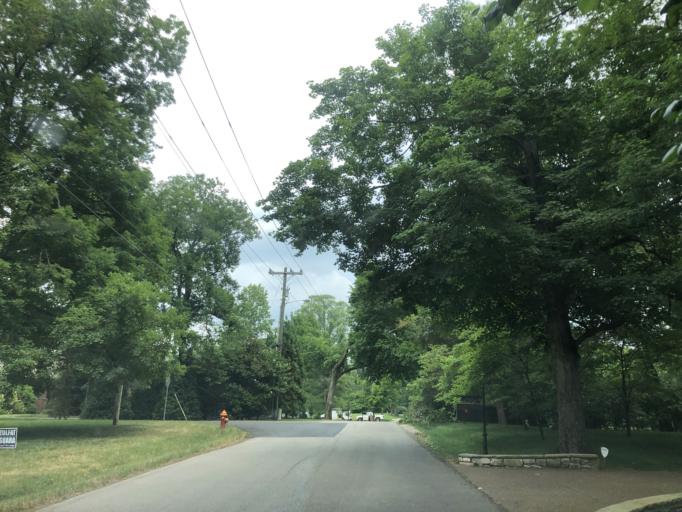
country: US
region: Tennessee
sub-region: Davidson County
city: Belle Meade
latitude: 36.1193
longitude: -86.8236
